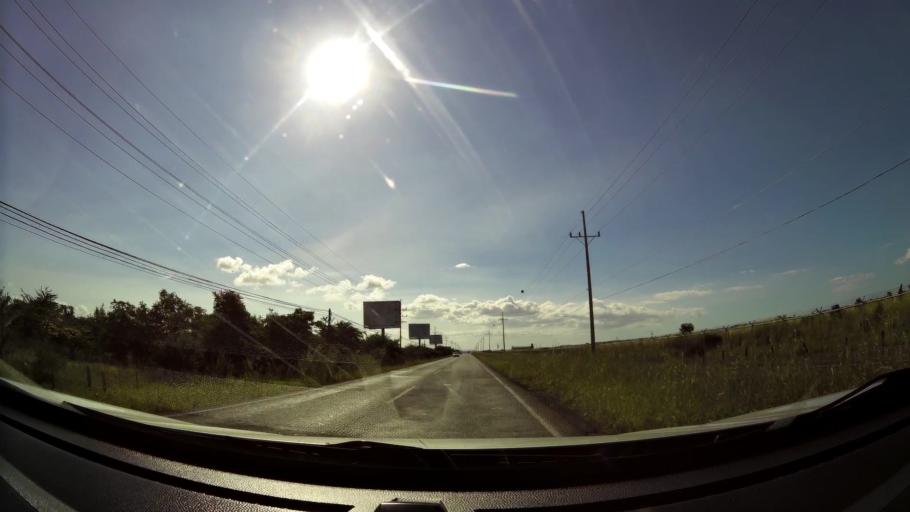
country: CR
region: Guanacaste
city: Liberia
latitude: 10.5901
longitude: -85.5454
